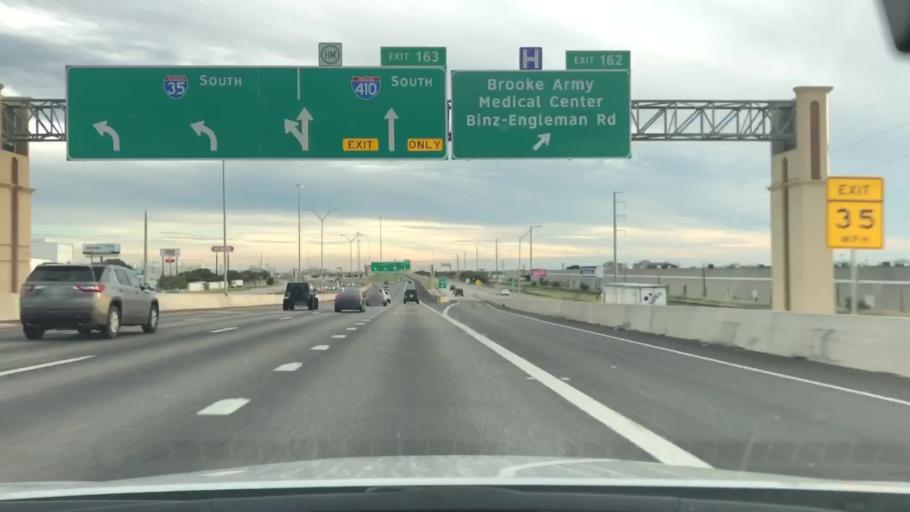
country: US
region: Texas
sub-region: Bexar County
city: Kirby
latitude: 29.4830
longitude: -98.4036
